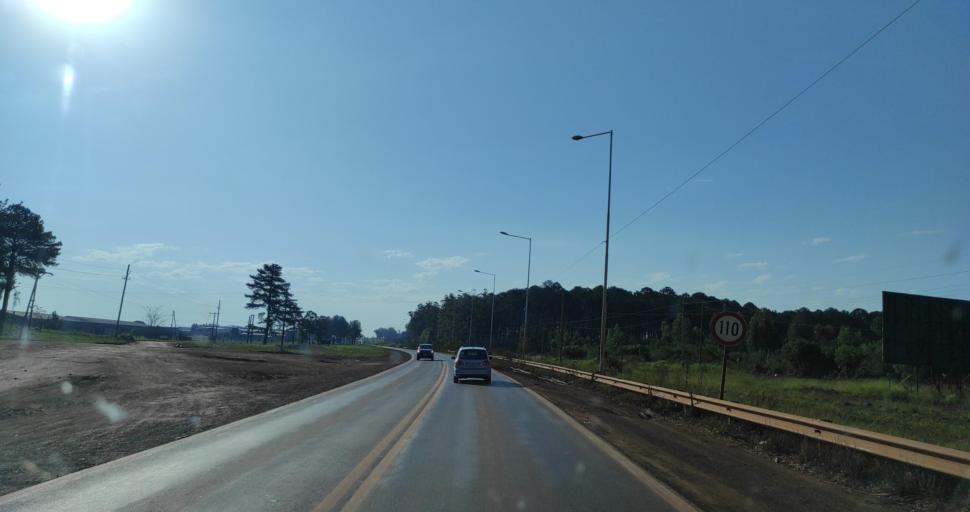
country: AR
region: Corrientes
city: Gobernador Ingeniero Valentin Virasoro
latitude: -28.0192
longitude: -56.0156
